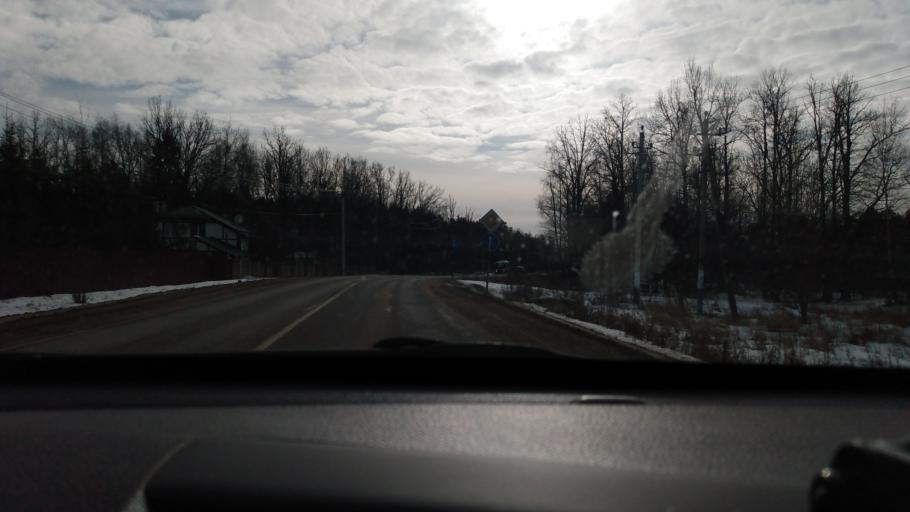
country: RU
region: Moskovskaya
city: Nakhabino
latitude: 55.8841
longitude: 37.1885
